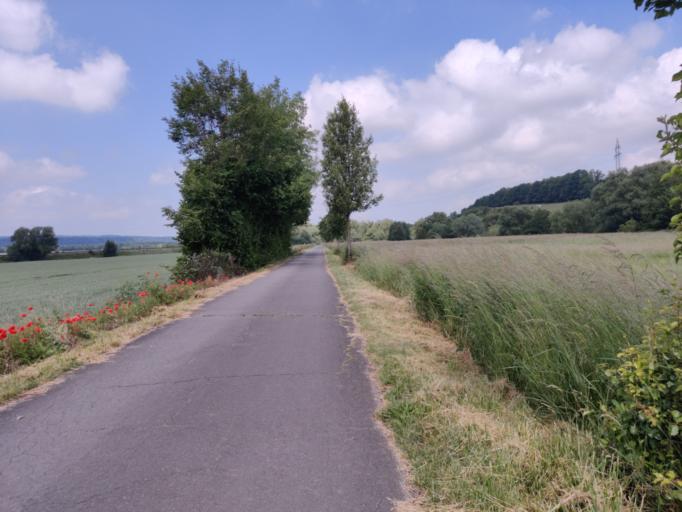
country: DE
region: Lower Saxony
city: Hildesheim
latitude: 52.1222
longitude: 9.9714
